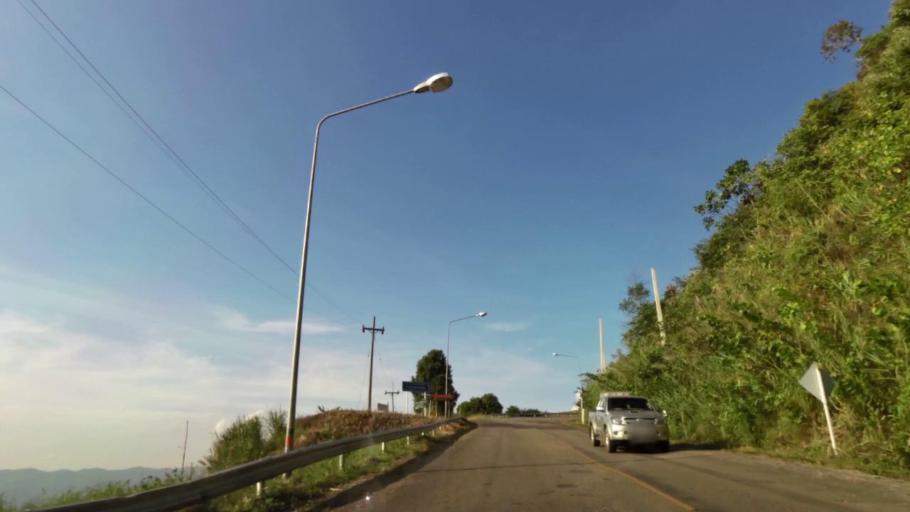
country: TH
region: Chiang Rai
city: Khun Tan
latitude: 19.8652
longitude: 100.4406
